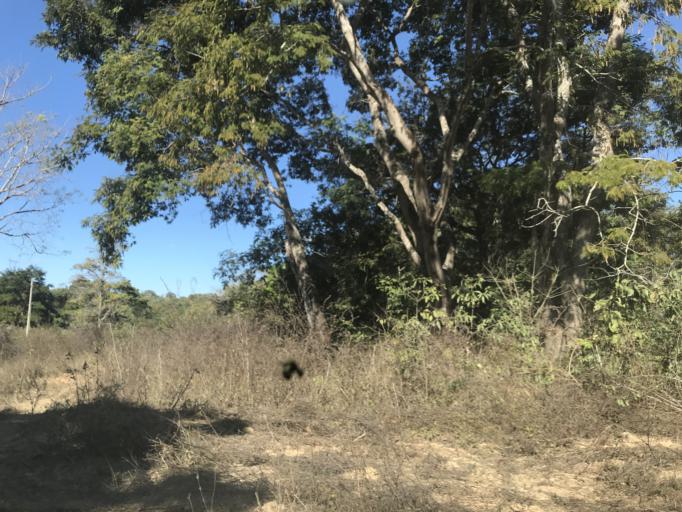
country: BR
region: Goias
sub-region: Padre Bernardo
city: Padre Bernardo
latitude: -15.4035
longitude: -48.2292
